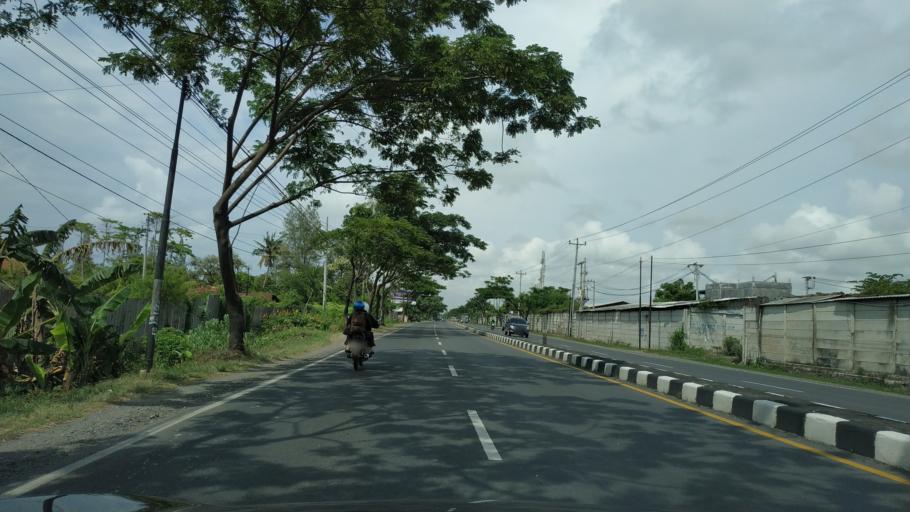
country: ID
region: Central Java
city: Tarub
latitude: -6.8724
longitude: 109.2453
